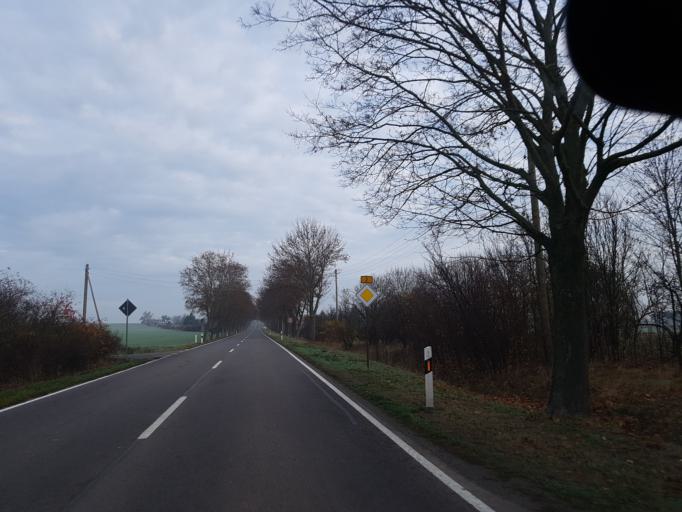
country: DE
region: Saxony-Anhalt
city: Kropstadt
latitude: 51.9678
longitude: 12.7555
